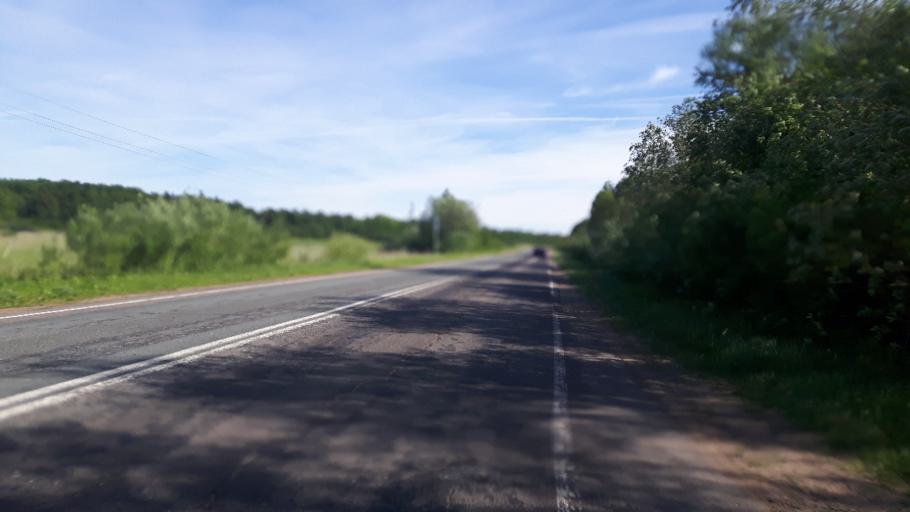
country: RU
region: Leningrad
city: Ivangorod
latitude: 59.4141
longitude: 28.3822
